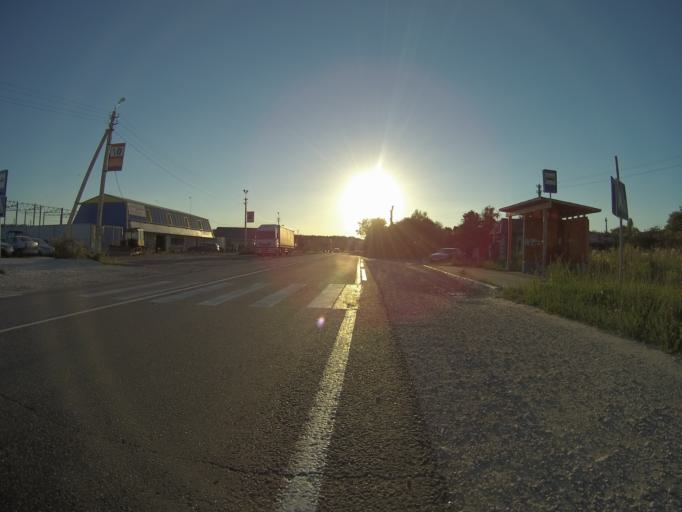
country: RU
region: Vladimir
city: Anopino
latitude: 55.7425
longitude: 40.7014
